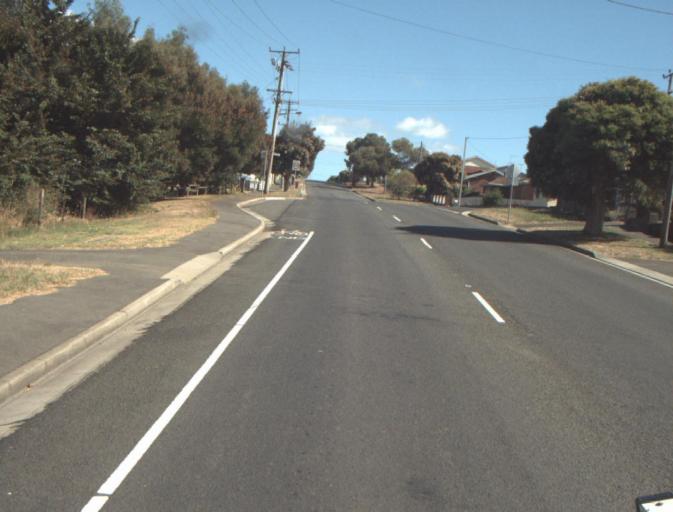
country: AU
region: Tasmania
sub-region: Launceston
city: Newstead
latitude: -41.4285
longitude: 147.1759
